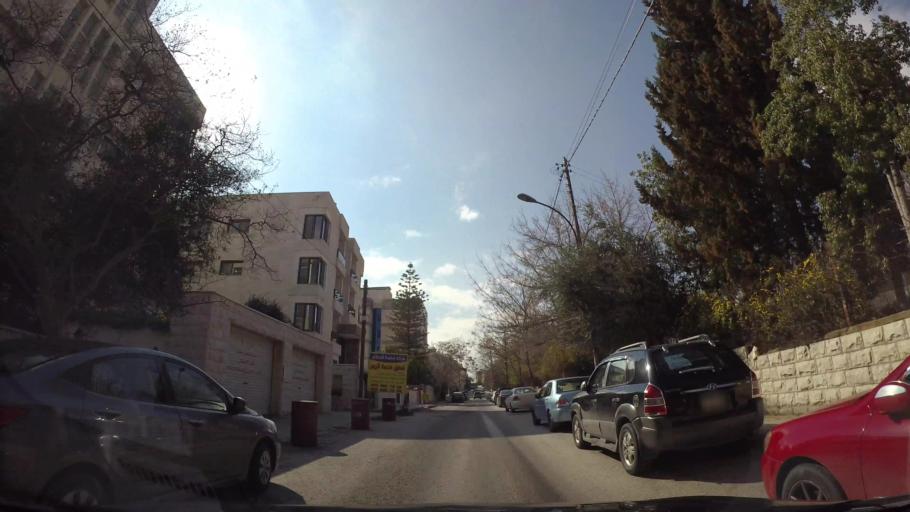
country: JO
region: Amman
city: Amman
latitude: 31.9704
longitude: 35.8932
